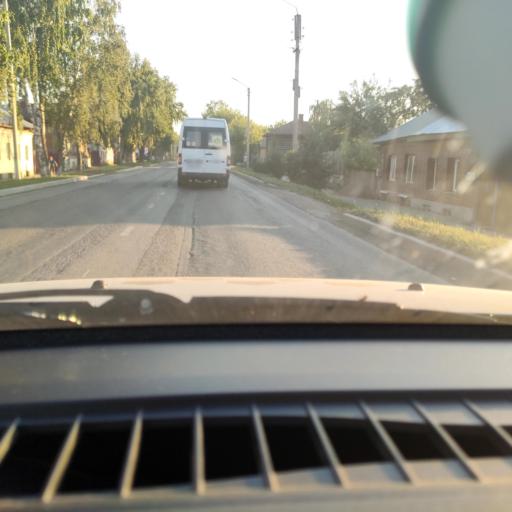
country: RU
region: Perm
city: Kungur
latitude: 57.4344
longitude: 56.9472
